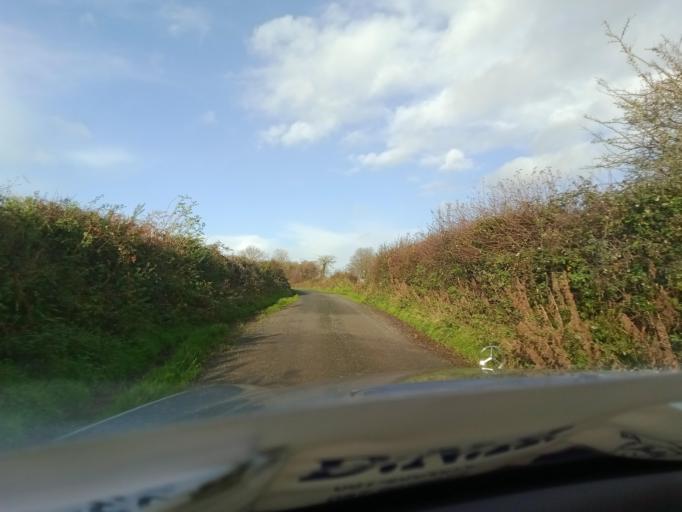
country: IE
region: Munster
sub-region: Waterford
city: Portlaw
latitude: 52.3163
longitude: -7.2873
